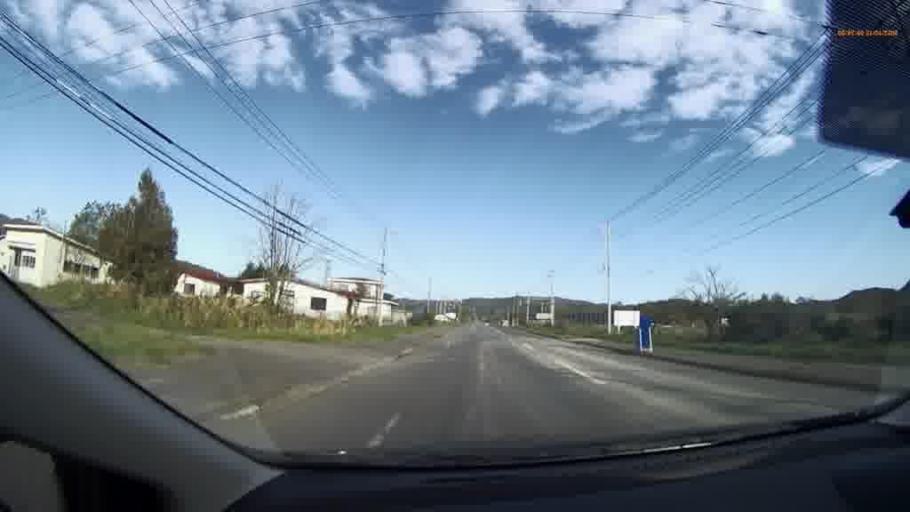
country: JP
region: Hokkaido
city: Kushiro
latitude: 42.9736
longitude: 144.0676
